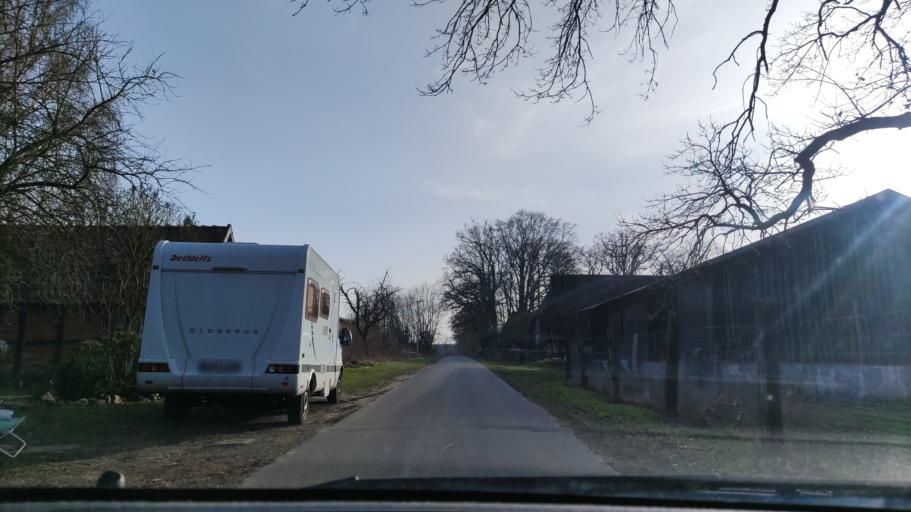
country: DE
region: Lower Saxony
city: Nahrendorf
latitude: 53.1786
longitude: 10.7835
